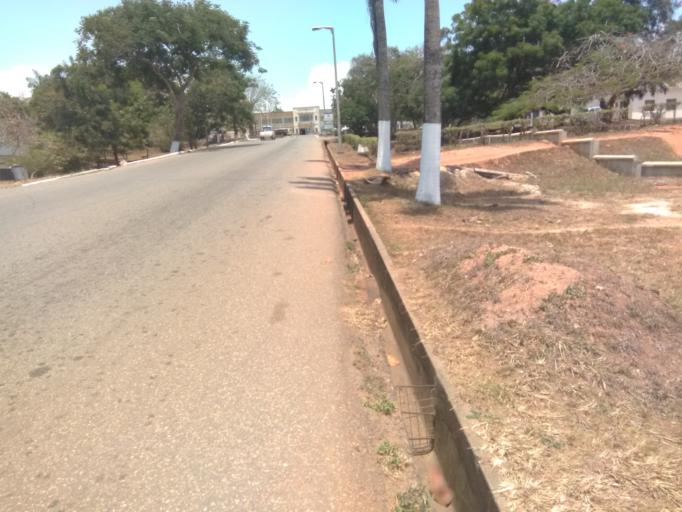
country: GH
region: Central
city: Cape Coast
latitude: 5.1040
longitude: -1.2842
